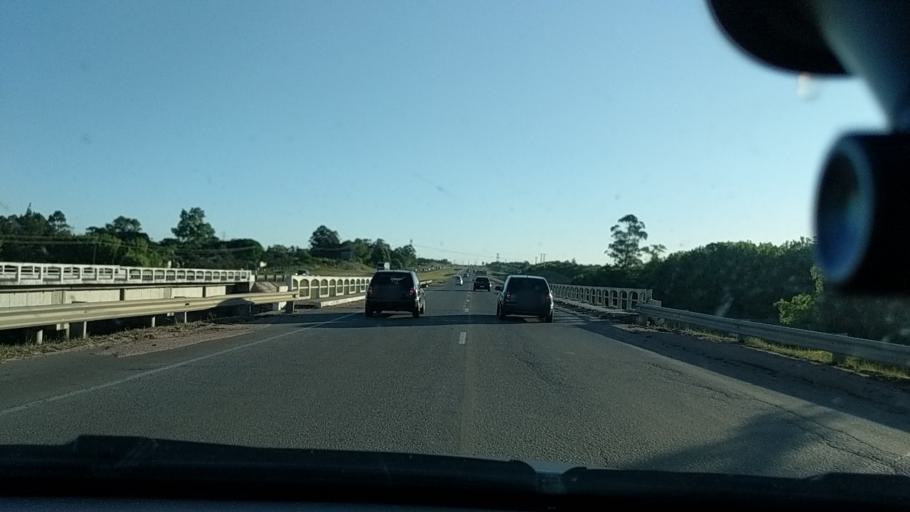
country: UY
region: Canelones
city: La Paz
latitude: -34.7535
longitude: -56.2575
